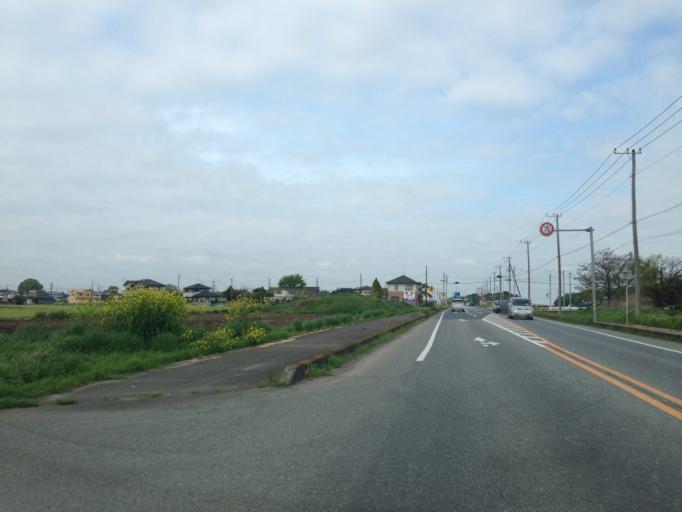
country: JP
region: Ibaraki
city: Ishige
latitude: 36.1480
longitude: 140.0204
